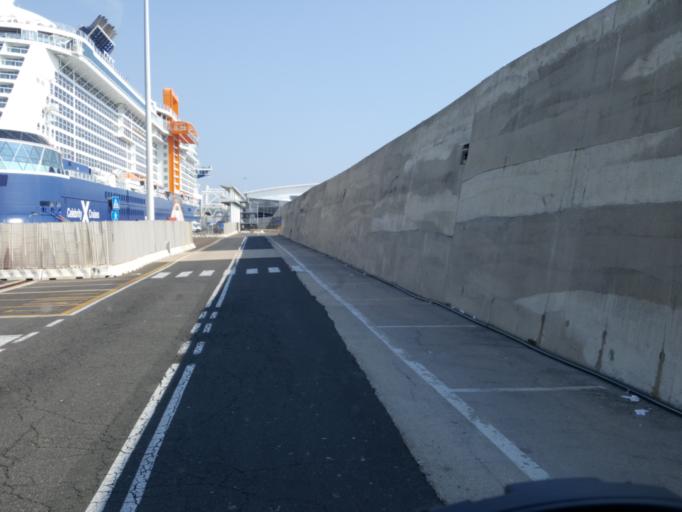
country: IT
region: Latium
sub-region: Citta metropolitana di Roma Capitale
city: Civitavecchia
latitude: 42.0974
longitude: 11.7756
